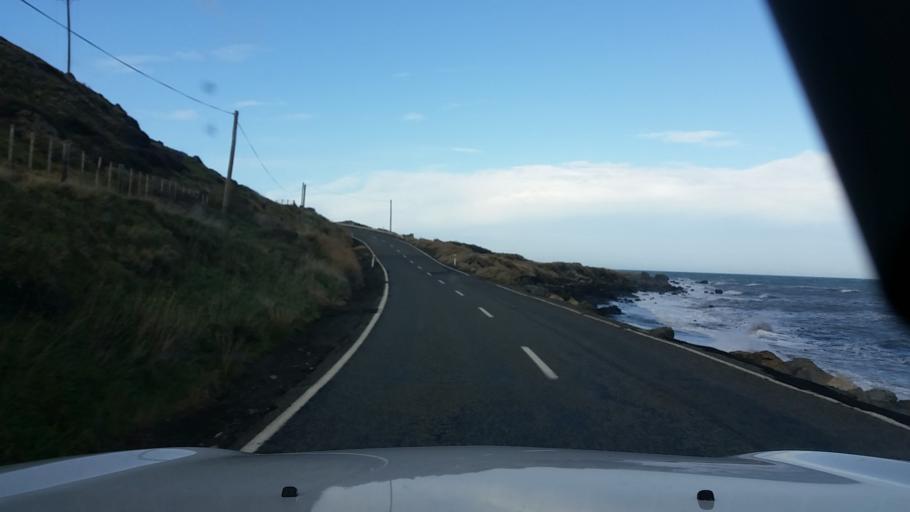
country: NZ
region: Wellington
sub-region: South Wairarapa District
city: Waipawa
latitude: -41.5421
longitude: 175.2186
